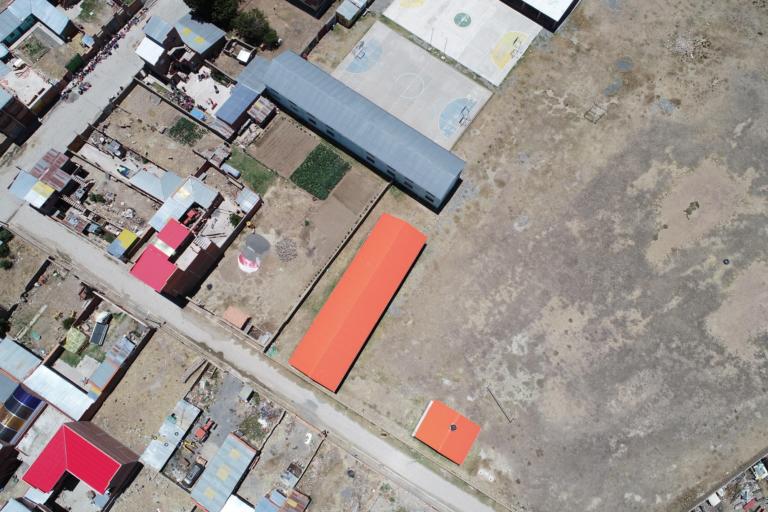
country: BO
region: La Paz
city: Achacachi
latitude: -16.0486
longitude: -68.6884
